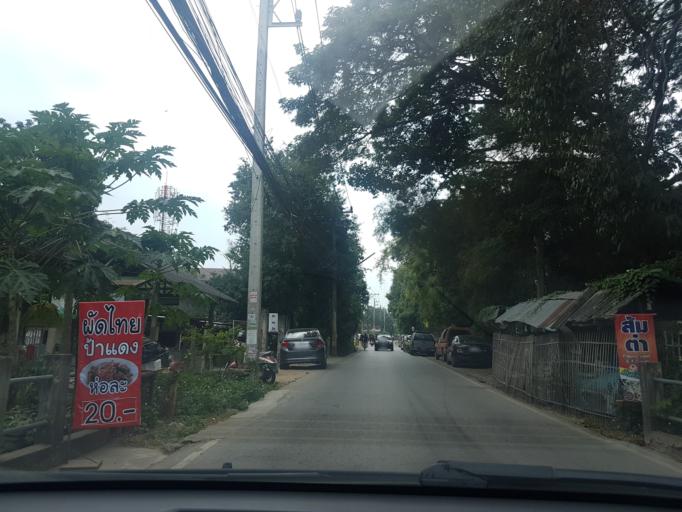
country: TH
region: Chiang Mai
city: Chiang Mai
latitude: 18.7821
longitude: 98.9539
